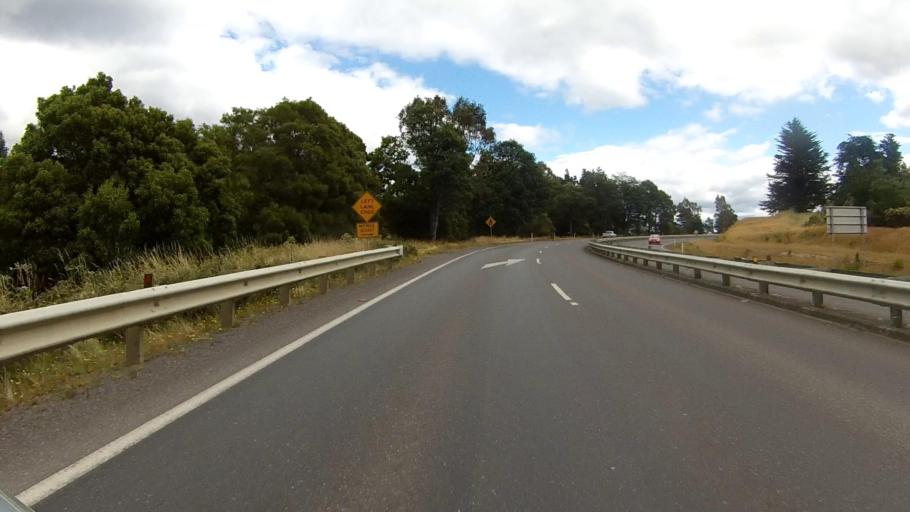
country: AU
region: Tasmania
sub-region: Kingborough
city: Margate
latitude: -42.9789
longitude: 147.1643
